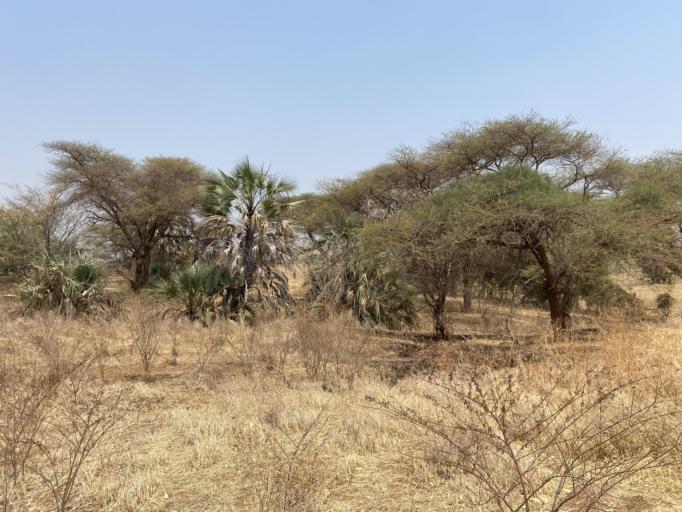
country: ZW
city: Chirundu
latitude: -16.1604
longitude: 28.8019
